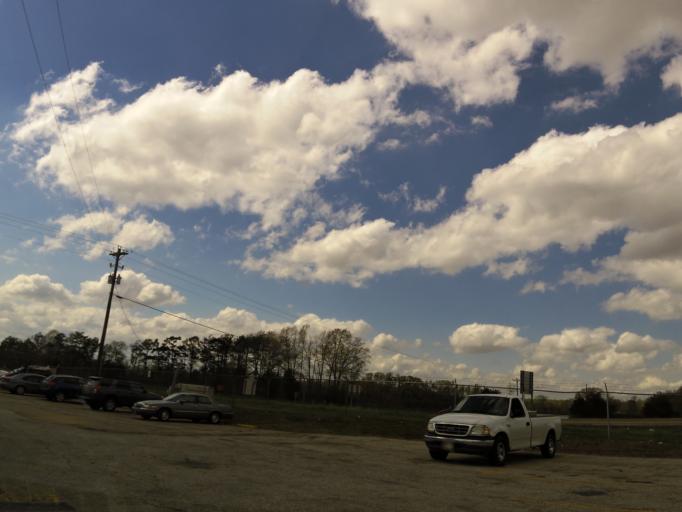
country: US
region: Tennessee
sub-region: Crockett County
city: Bells
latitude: 35.5960
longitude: -89.0549
